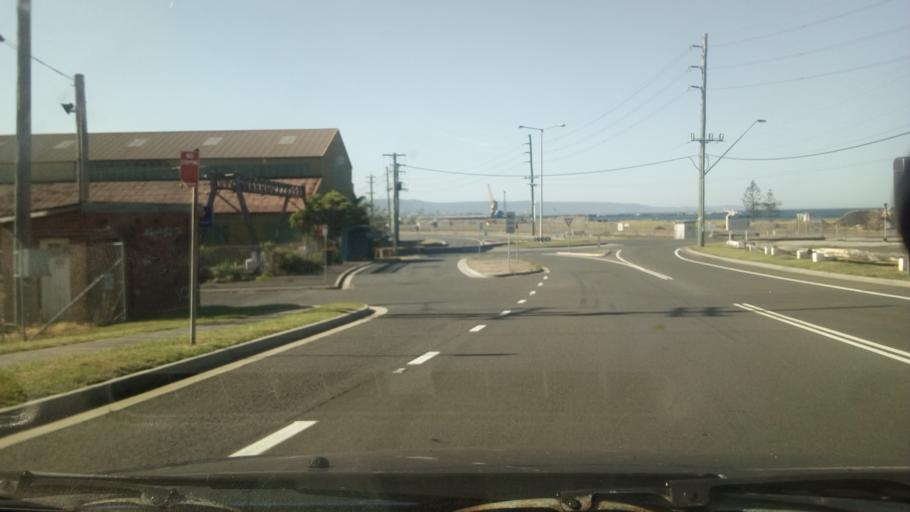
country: AU
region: New South Wales
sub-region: Wollongong
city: Port Kembla
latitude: -34.4776
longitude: 150.9039
